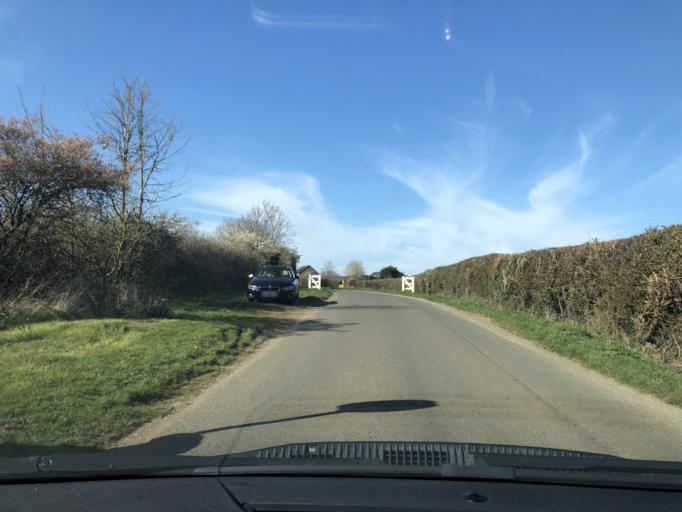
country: GB
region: England
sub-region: Oxfordshire
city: Hook Norton
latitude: 51.9978
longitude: -1.4901
